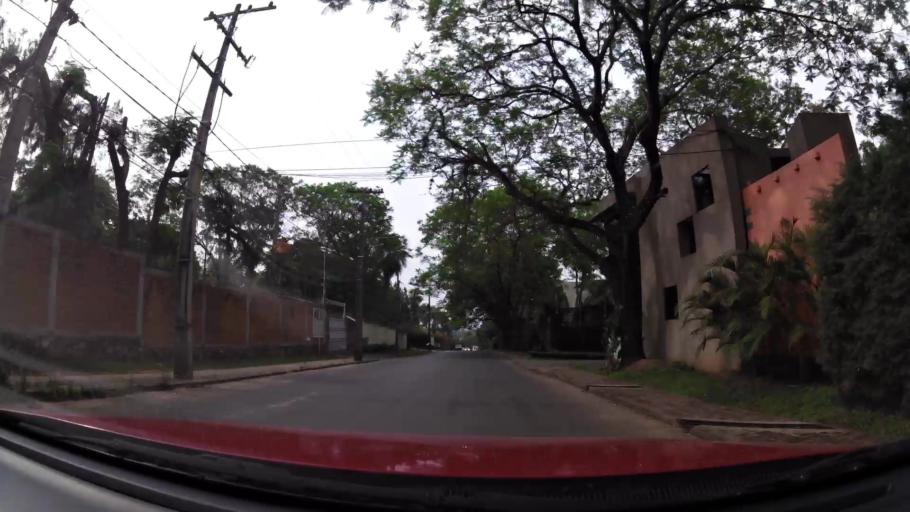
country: PY
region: Central
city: Fernando de la Mora
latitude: -25.2826
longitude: -57.5529
